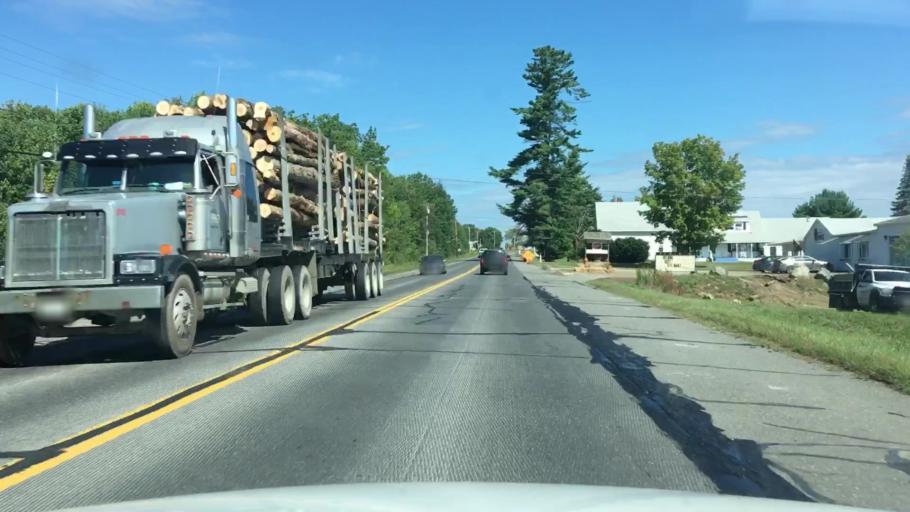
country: US
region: Maine
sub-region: Penobscot County
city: Newport
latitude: 44.8557
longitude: -69.2835
